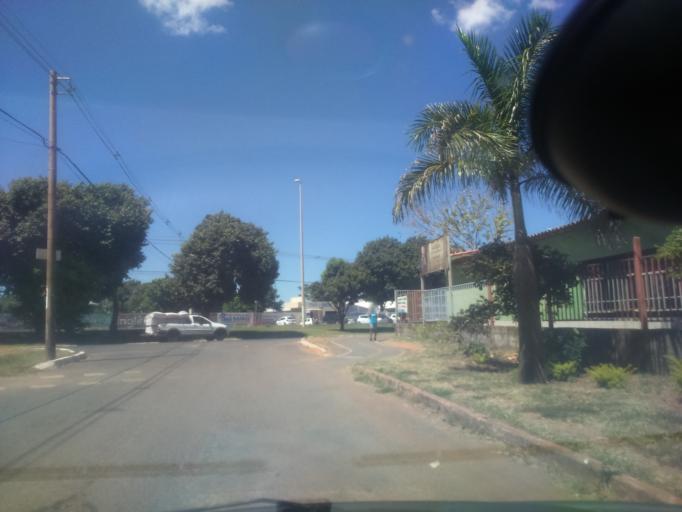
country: BR
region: Federal District
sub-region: Brasilia
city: Brasilia
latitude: -15.9984
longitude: -48.0534
